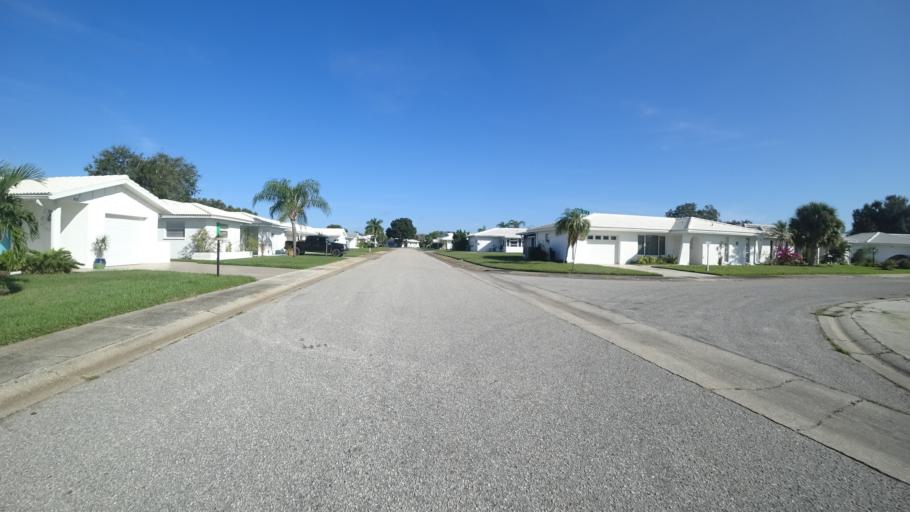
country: US
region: Florida
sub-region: Manatee County
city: Ellenton
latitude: 27.4957
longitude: -82.5117
